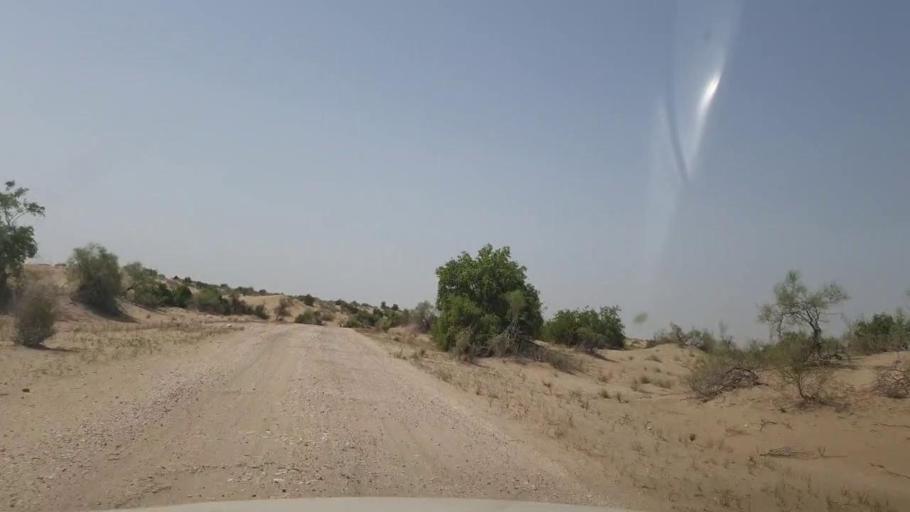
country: PK
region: Sindh
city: Khanpur
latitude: 27.4111
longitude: 69.3196
